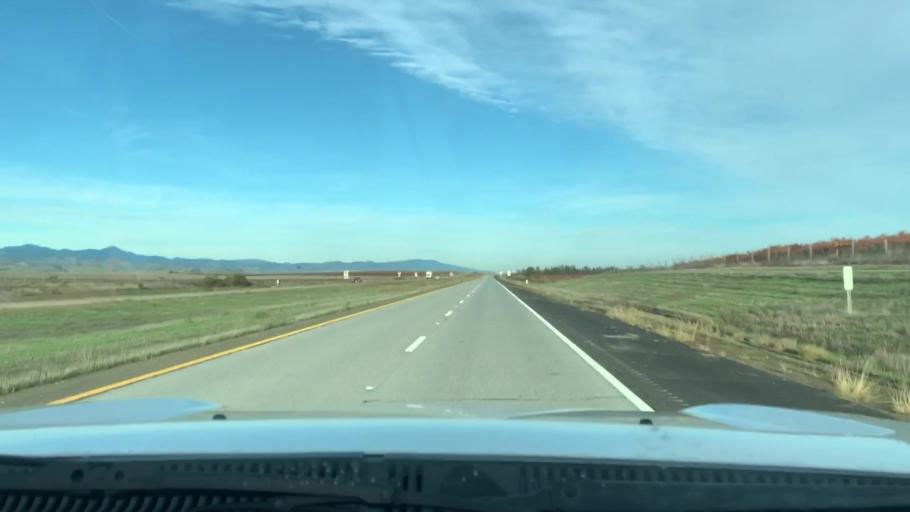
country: US
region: California
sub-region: Monterey County
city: King City
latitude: 36.0550
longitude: -120.9717
